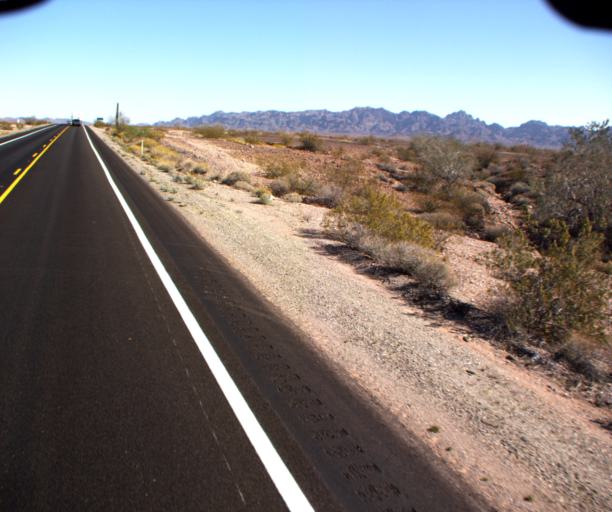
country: US
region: Arizona
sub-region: Yuma County
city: Wellton
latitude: 33.1153
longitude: -114.2938
